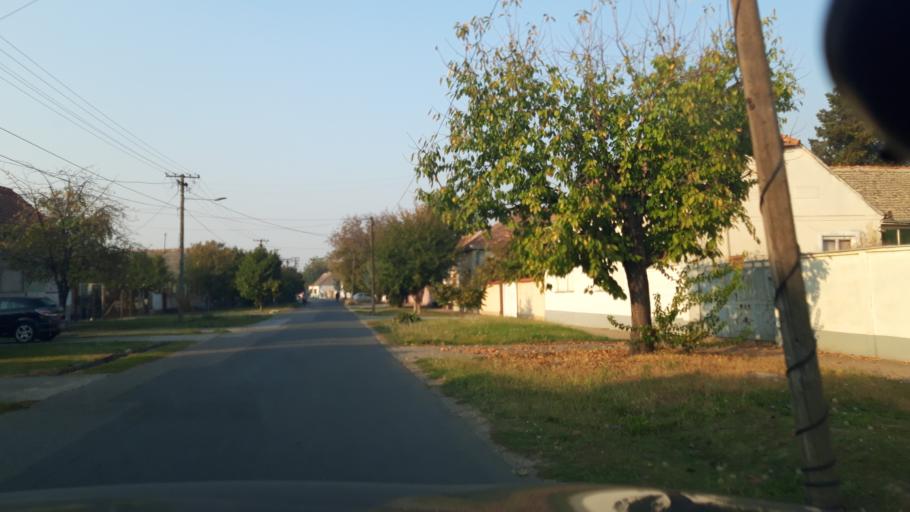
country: RS
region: Autonomna Pokrajina Vojvodina
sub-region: Sremski Okrug
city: Stara Pazova
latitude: 44.9890
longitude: 20.1495
